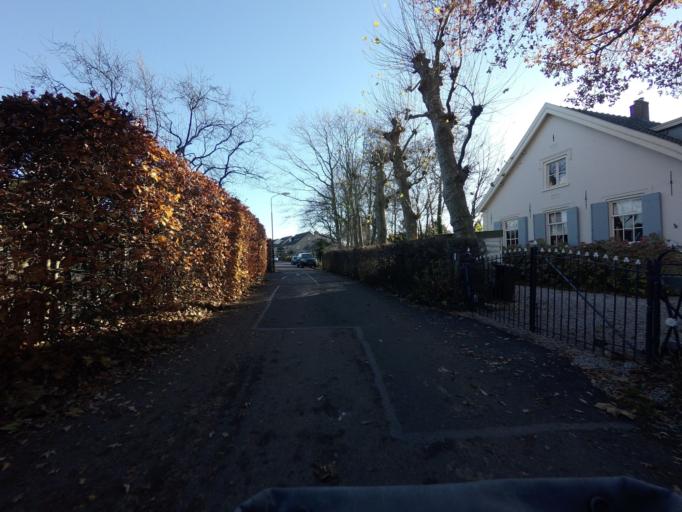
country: NL
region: Utrecht
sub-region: Stichtse Vecht
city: Vreeland
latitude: 52.2480
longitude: 4.9871
